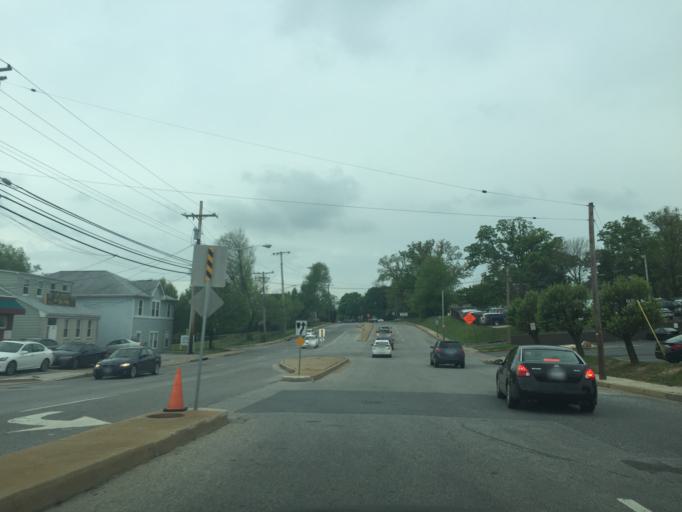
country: US
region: Maryland
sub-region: Baltimore County
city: Catonsville
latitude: 39.2876
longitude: -76.7314
